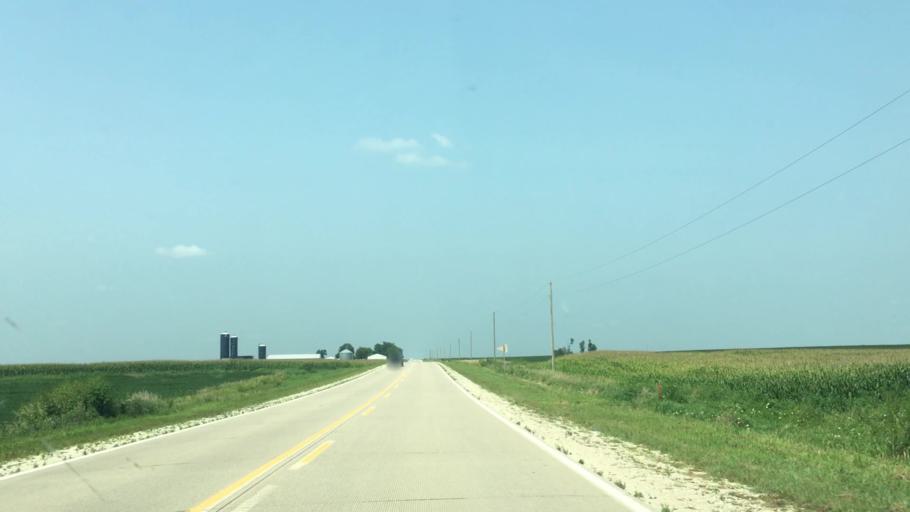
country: US
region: Iowa
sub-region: Fayette County
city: Fayette
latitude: 42.7369
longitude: -91.8040
